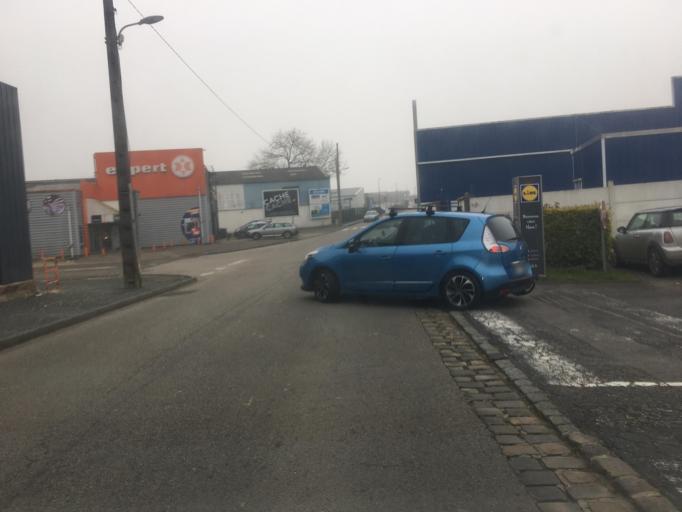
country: FR
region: Haute-Normandie
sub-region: Departement de la Seine-Maritime
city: Neufchatel-en-Bray
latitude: 49.7329
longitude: 1.4343
